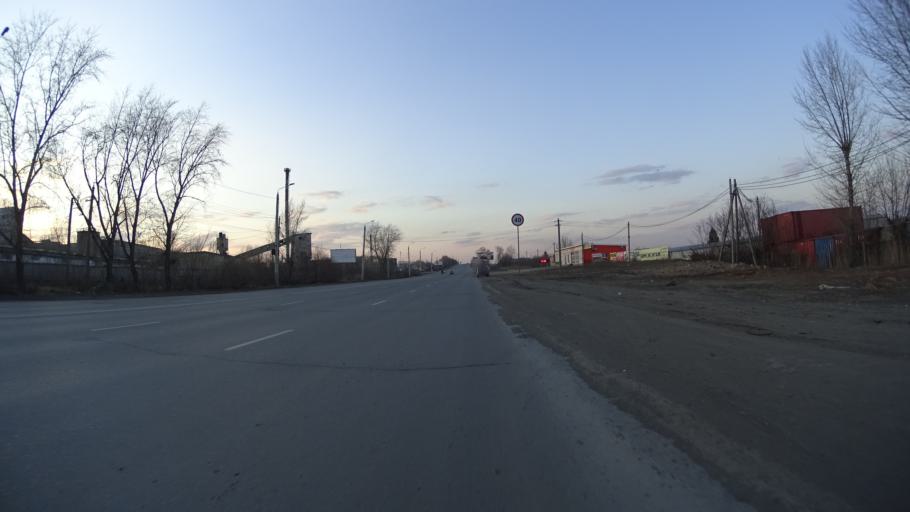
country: RU
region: Chelyabinsk
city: Novosineglazovskiy
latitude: 55.0959
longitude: 61.3880
